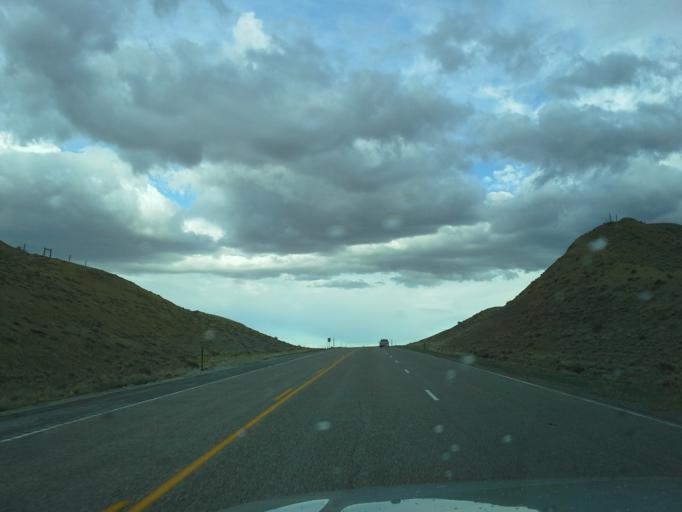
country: US
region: Wyoming
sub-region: Big Horn County
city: Lovell
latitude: 44.7880
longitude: -108.3615
